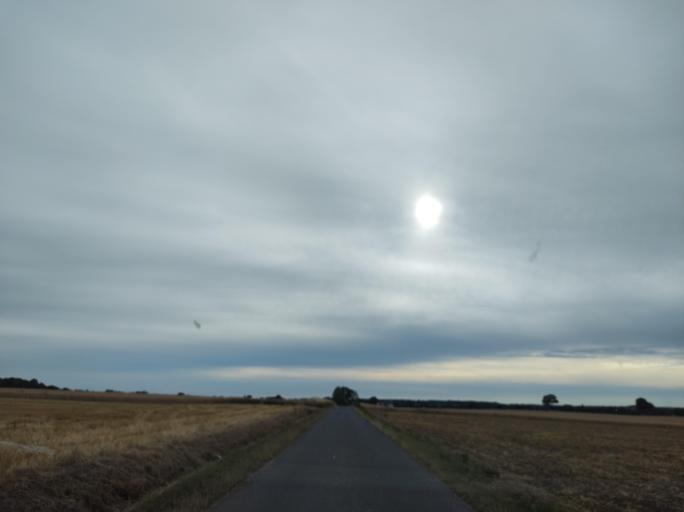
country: DE
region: North Rhine-Westphalia
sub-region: Regierungsbezirk Detmold
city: Salzkotten
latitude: 51.6518
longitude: 8.6230
